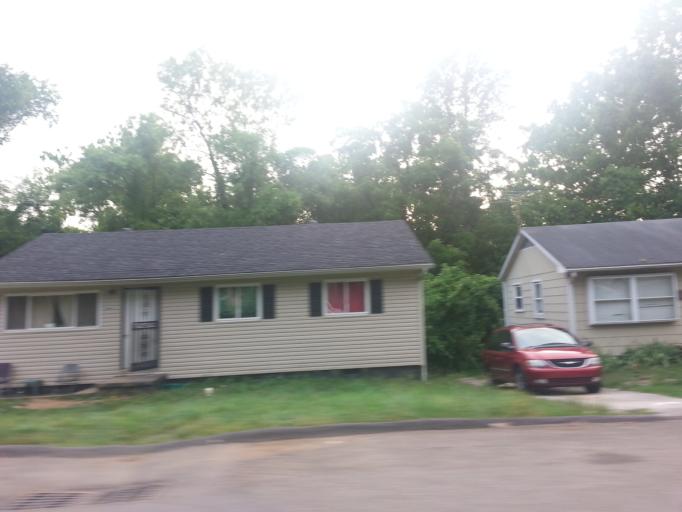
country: US
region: Tennessee
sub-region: Knox County
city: Knoxville
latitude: 35.9818
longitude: -83.8866
